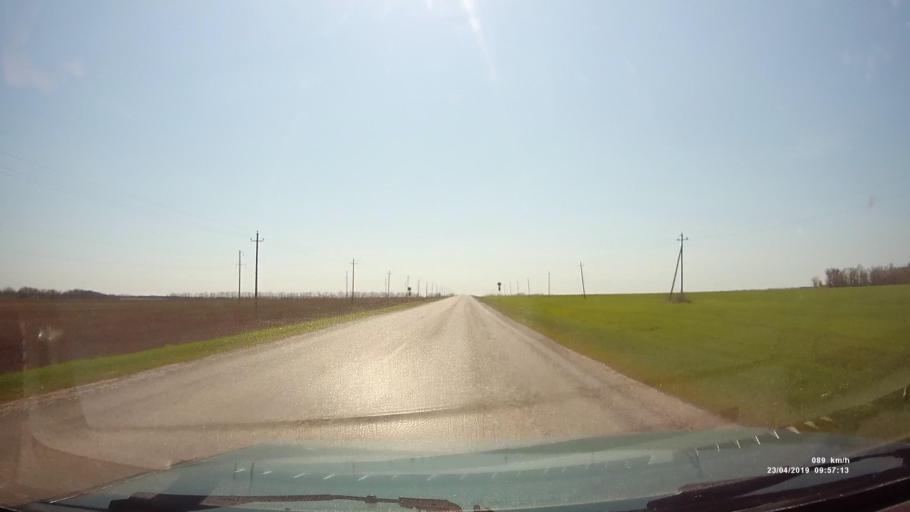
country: RU
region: Rostov
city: Orlovskiy
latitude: 46.7909
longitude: 42.0826
